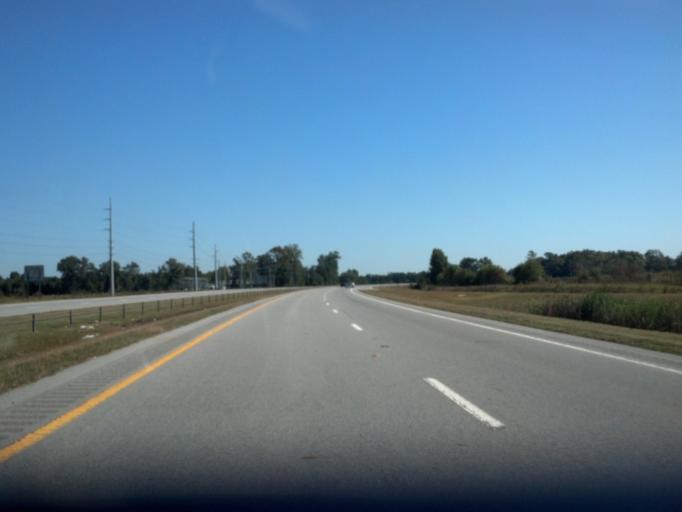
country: US
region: North Carolina
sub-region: Pitt County
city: Greenville
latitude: 35.6618
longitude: -77.4097
